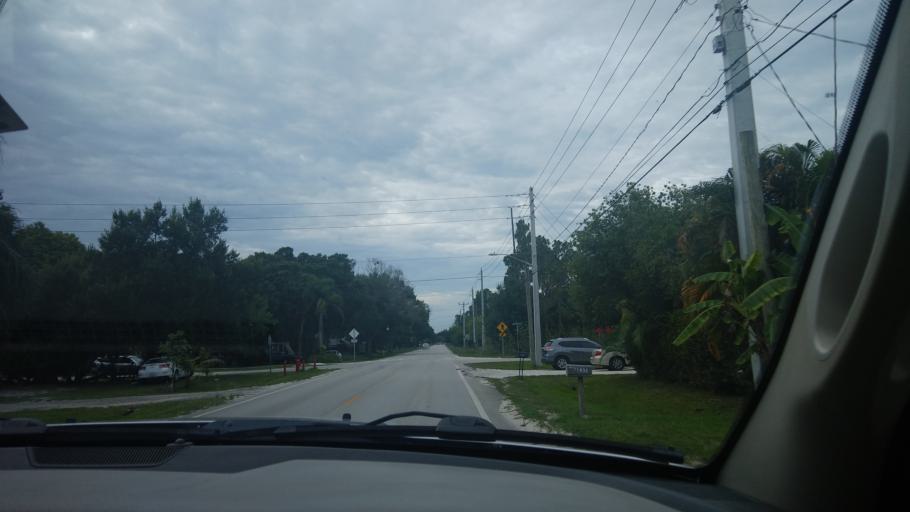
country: US
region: Florida
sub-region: Indian River County
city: Fellsmere
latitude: 27.7584
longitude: -80.5933
